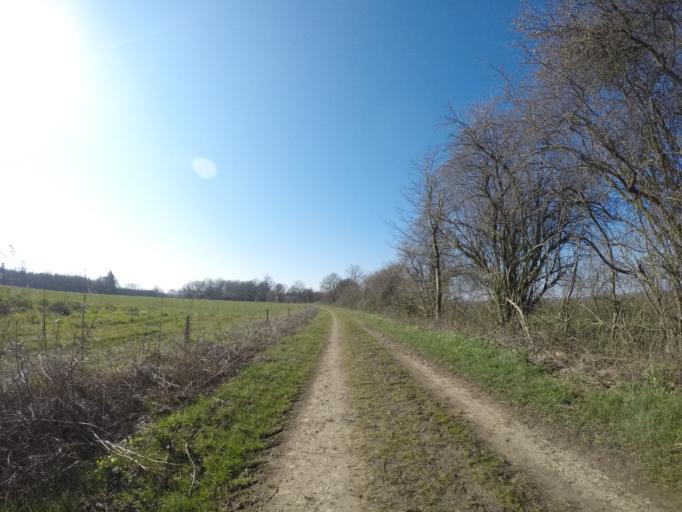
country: BE
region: Wallonia
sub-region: Province du Luxembourg
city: Habay-la-Vieille
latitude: 49.7076
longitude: 5.5974
